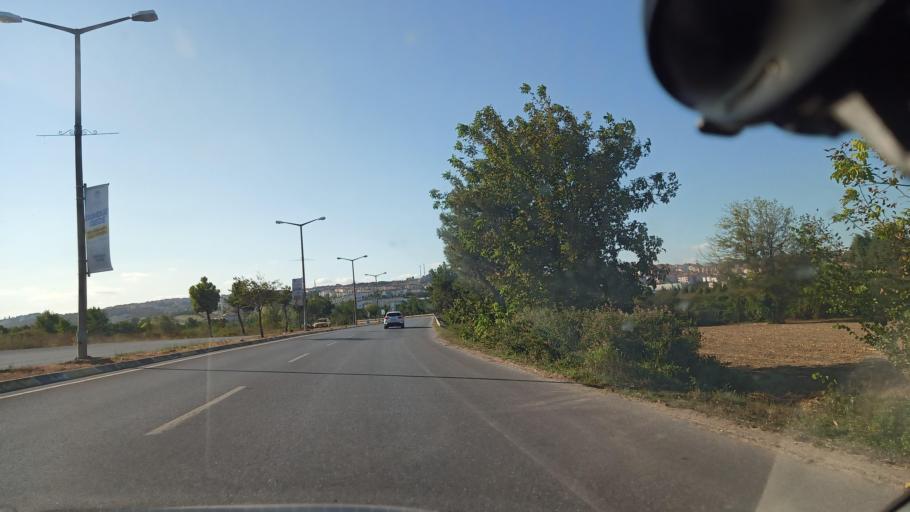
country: TR
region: Sakarya
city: Kazimpasa
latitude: 40.8467
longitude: 30.3266
